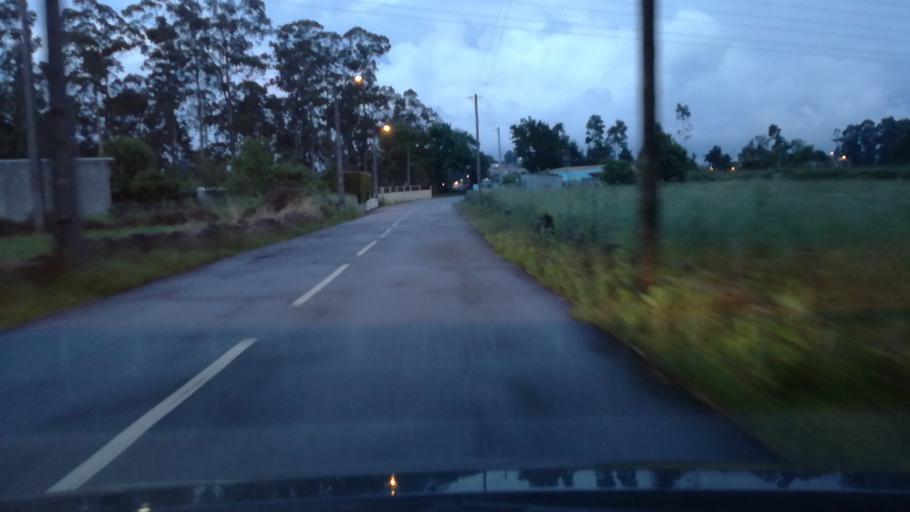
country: PT
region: Porto
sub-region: Maia
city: Maia
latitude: 41.2533
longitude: -8.6120
